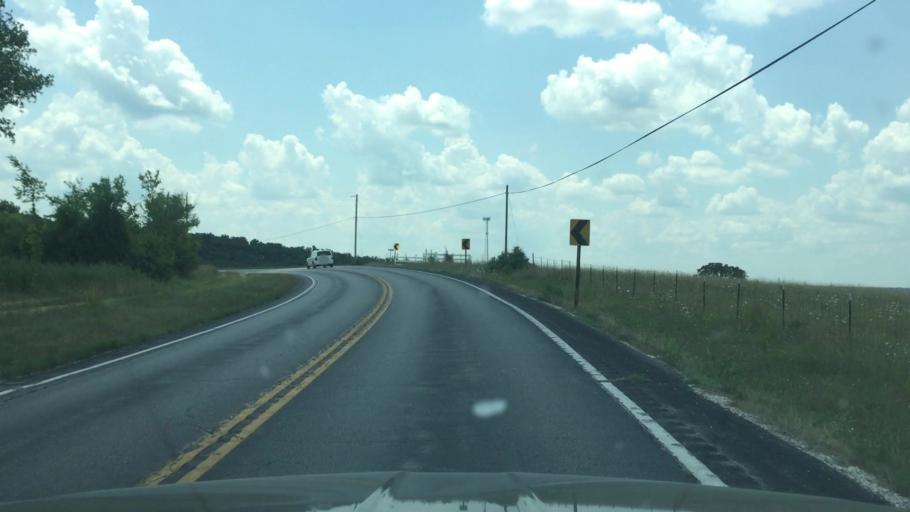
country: US
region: Missouri
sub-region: Miller County
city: Tuscumbia
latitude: 38.1020
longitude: -92.4987
